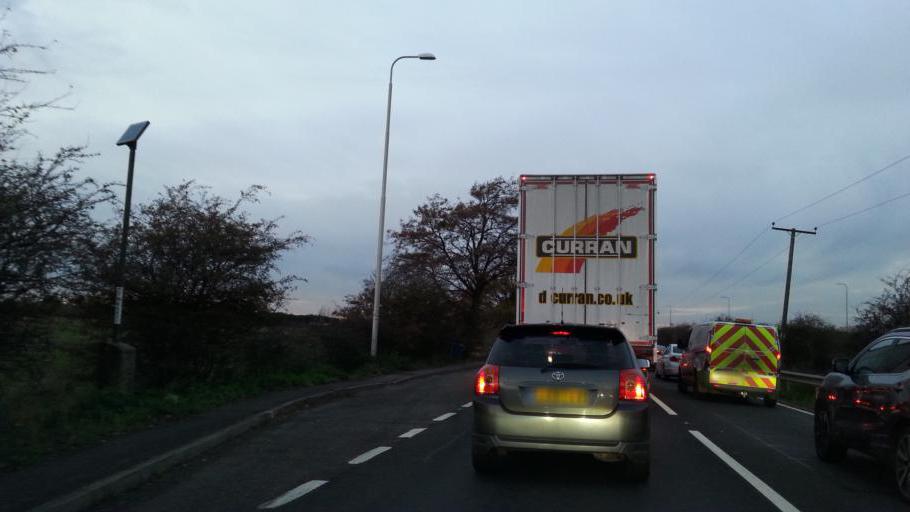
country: GB
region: England
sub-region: Bedford
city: Roxton
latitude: 52.1790
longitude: -0.3043
